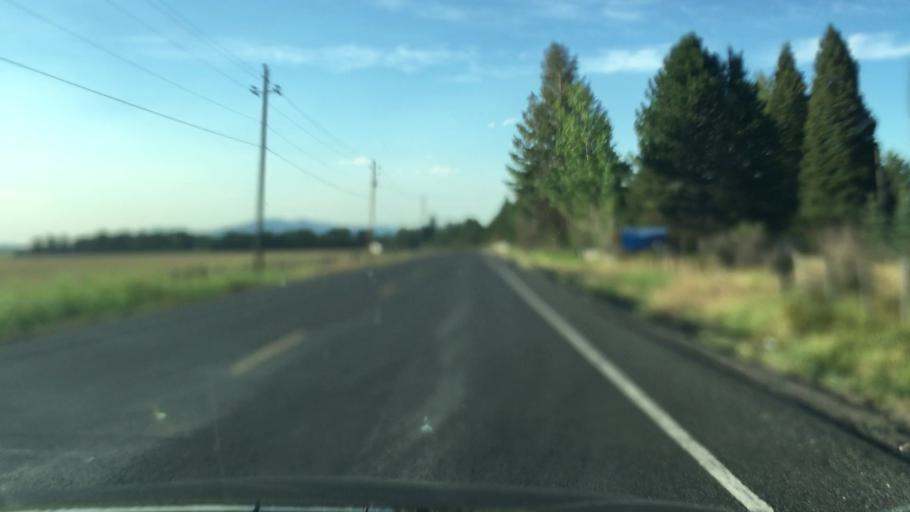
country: US
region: Idaho
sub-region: Valley County
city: McCall
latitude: 44.8182
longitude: -116.0781
